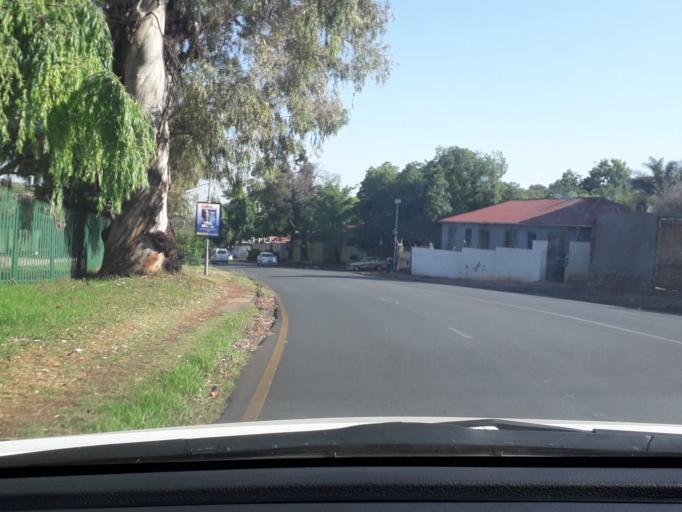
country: ZA
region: Gauteng
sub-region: City of Johannesburg Metropolitan Municipality
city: Johannesburg
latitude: -26.1738
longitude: 28.0004
